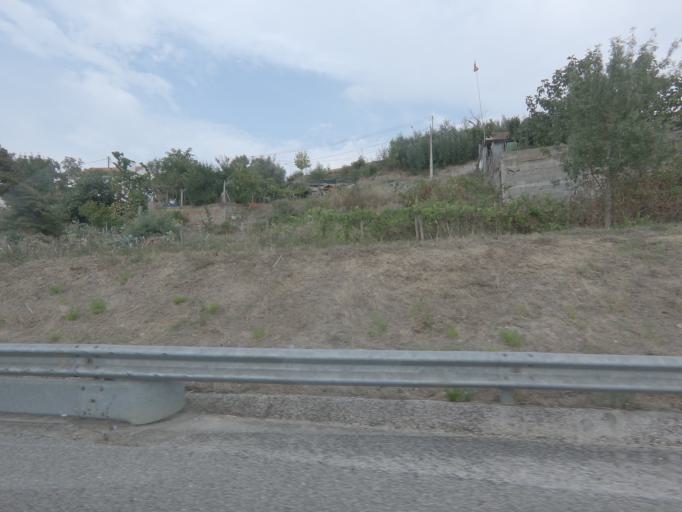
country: PT
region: Coimbra
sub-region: Coimbra
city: Coimbra
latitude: 40.2119
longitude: -8.4462
